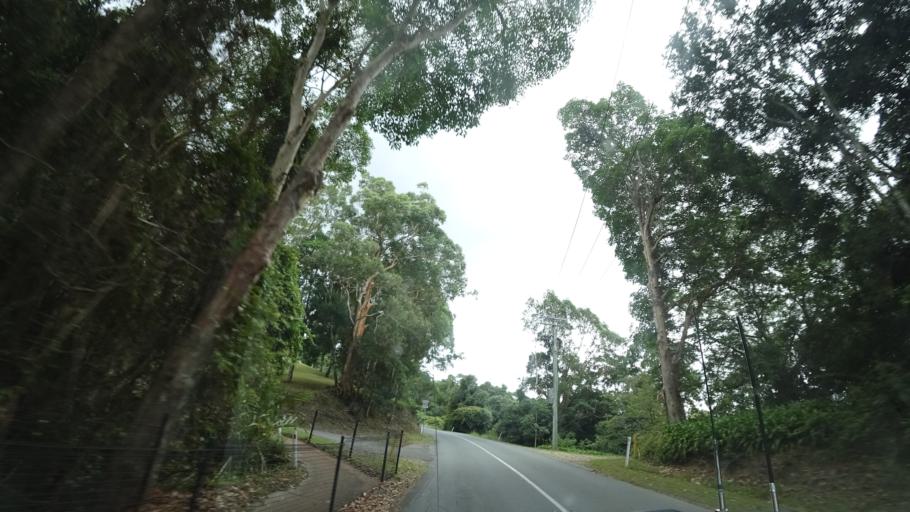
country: AU
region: Queensland
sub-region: Moreton Bay
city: Highvale
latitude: -27.3944
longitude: 152.7804
